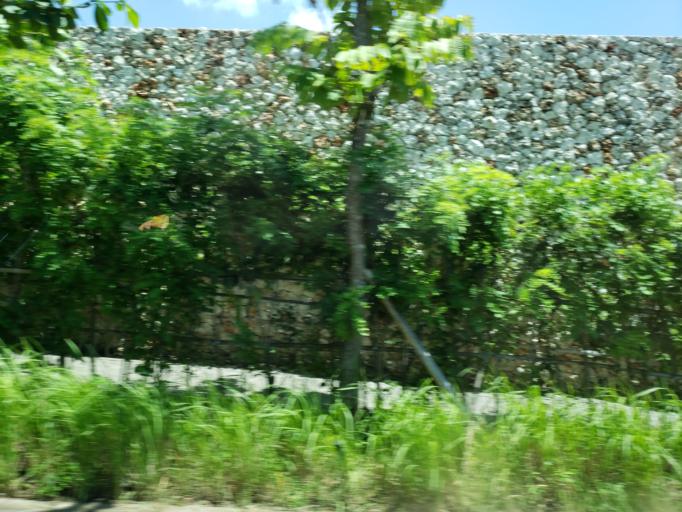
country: ID
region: Bali
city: Kangin
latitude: -8.8454
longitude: 115.1407
